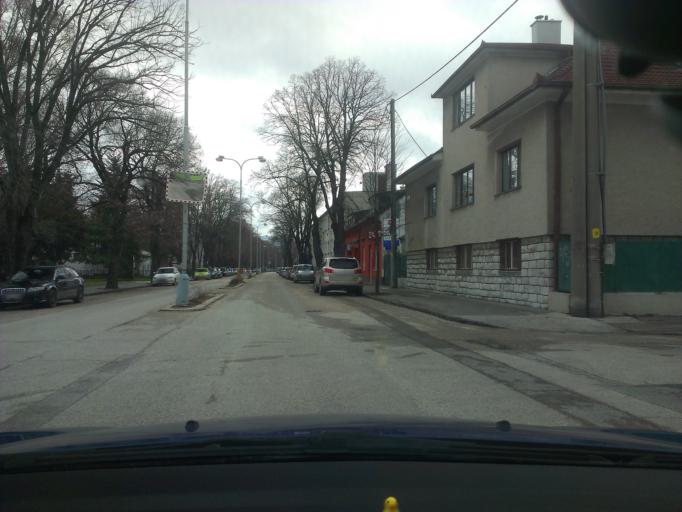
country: SK
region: Trnavsky
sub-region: Okres Trnava
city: Piestany
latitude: 48.5954
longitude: 17.8185
